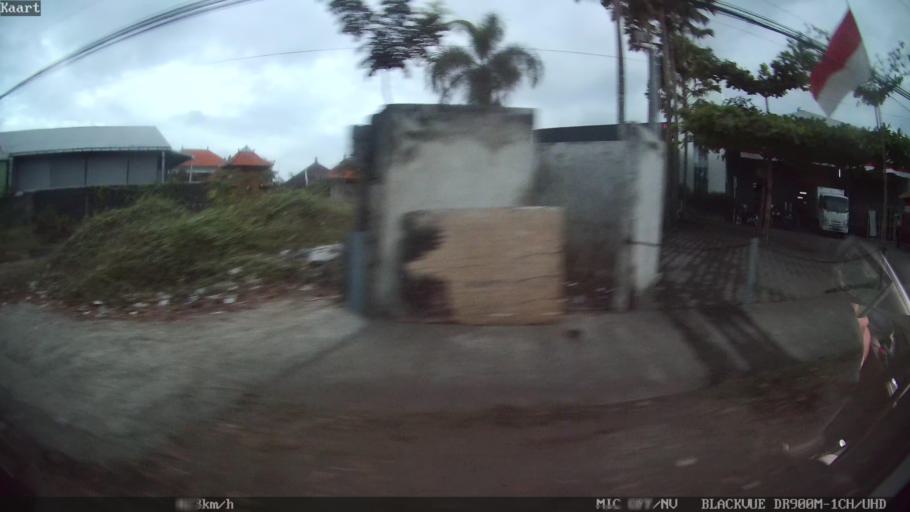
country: ID
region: Bali
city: Banjar Pasekan
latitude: -8.6273
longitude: 115.2948
